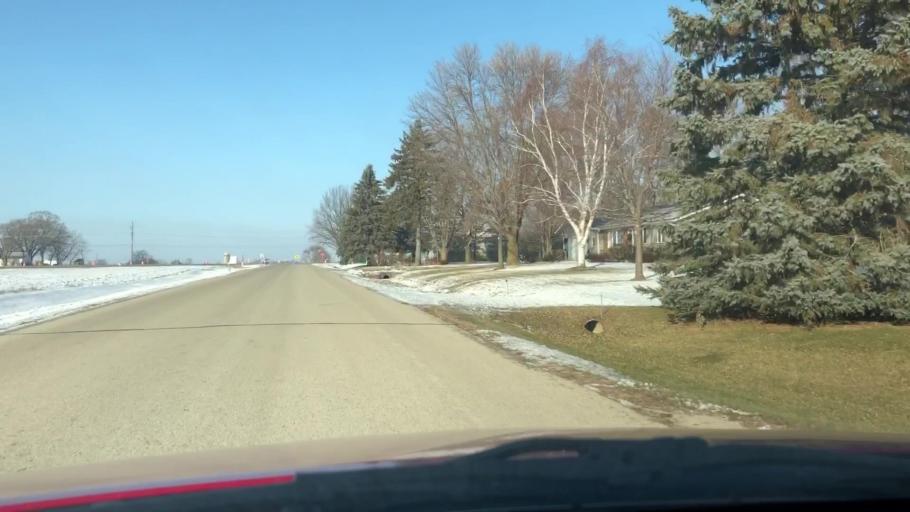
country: US
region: Wisconsin
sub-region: Outagamie County
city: Seymour
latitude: 44.4984
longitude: -88.3089
